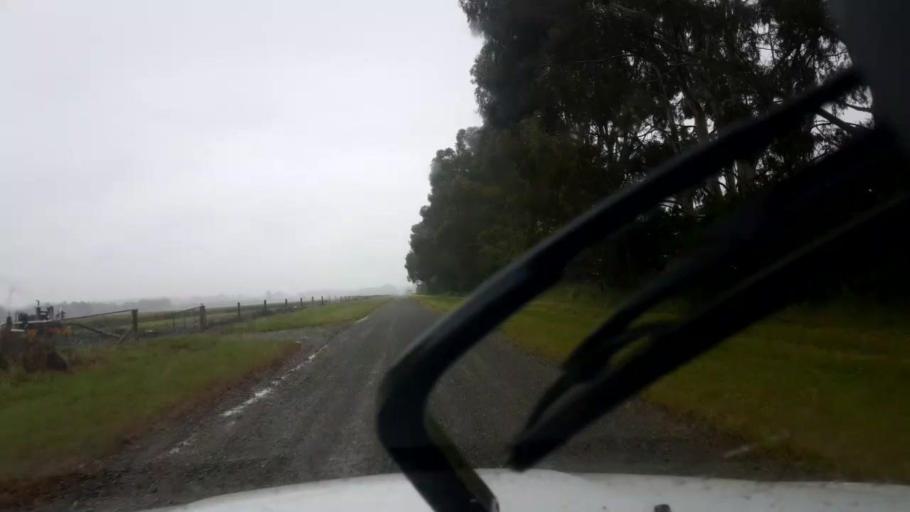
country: NZ
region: Canterbury
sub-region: Timaru District
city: Pleasant Point
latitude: -44.2880
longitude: 171.2101
